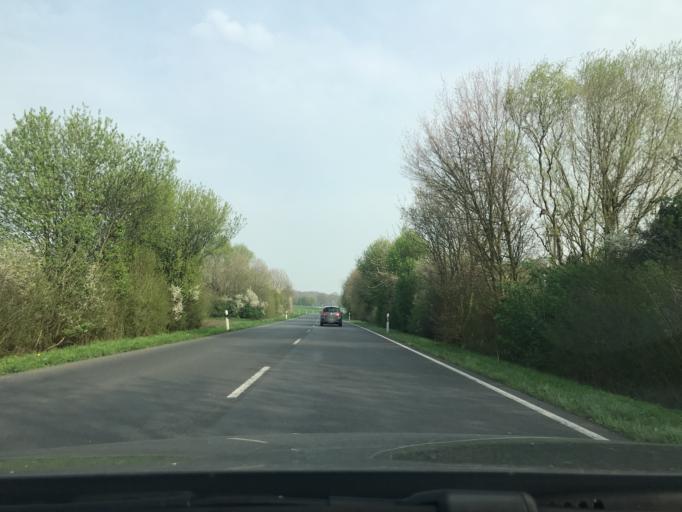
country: DE
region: North Rhine-Westphalia
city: Geldern
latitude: 51.4965
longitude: 6.3241
